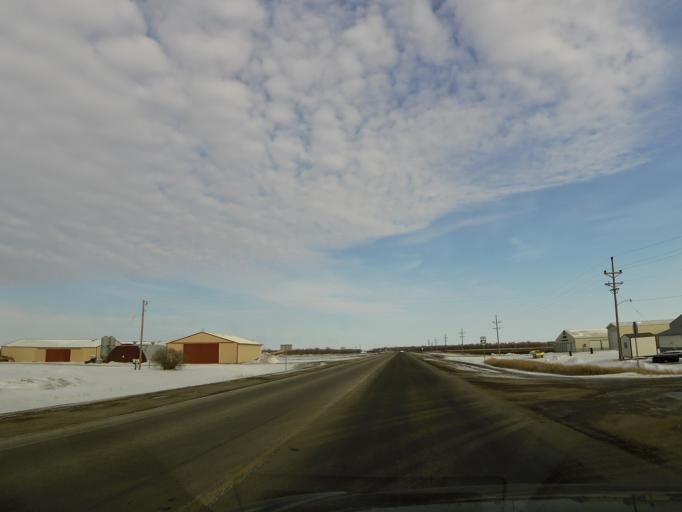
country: US
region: North Dakota
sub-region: Walsh County
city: Grafton
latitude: 48.5713
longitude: -97.1769
